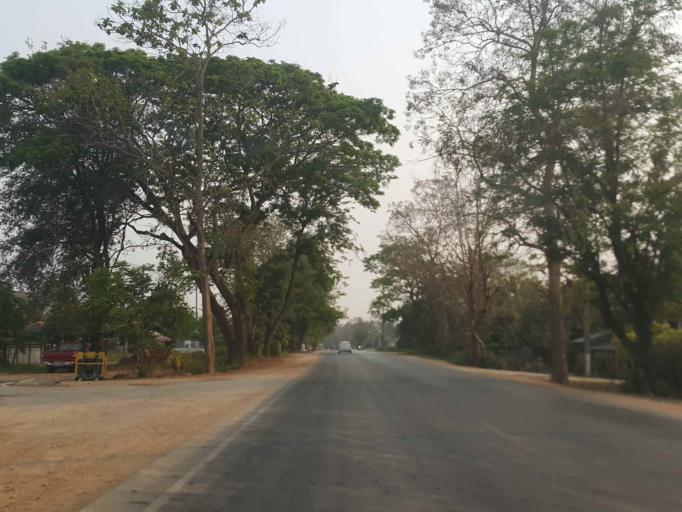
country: TH
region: Chiang Mai
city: San Sai
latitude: 18.9484
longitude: 98.9841
